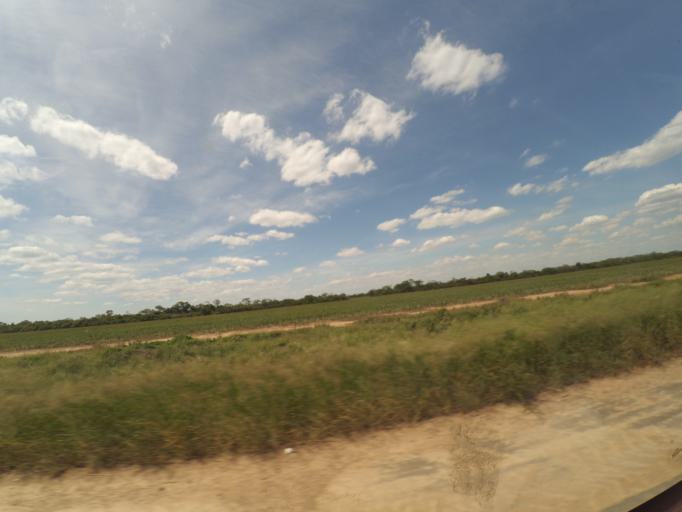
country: BO
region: Santa Cruz
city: Pailon
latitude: -17.5898
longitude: -61.9750
